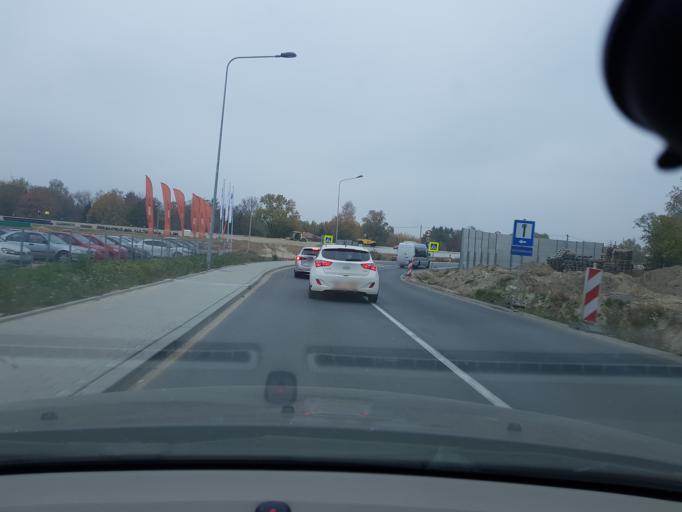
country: PL
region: Masovian Voivodeship
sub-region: Powiat pruszkowski
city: Nadarzyn
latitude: 52.0949
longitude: 20.8149
